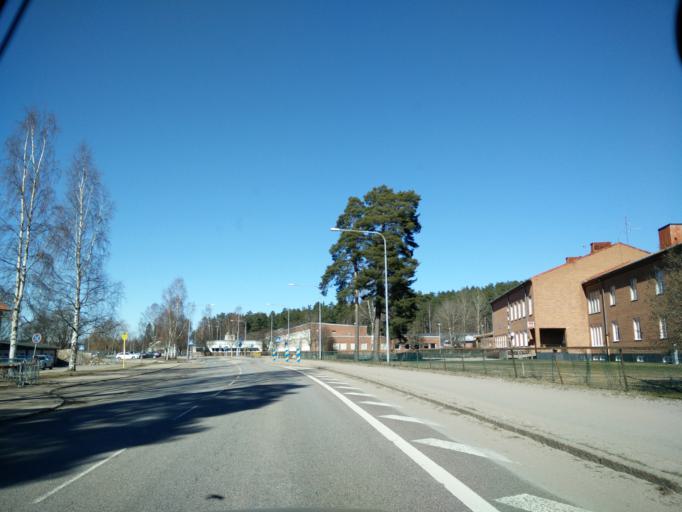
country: SE
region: Vaermland
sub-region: Hagfors Kommun
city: Hagfors
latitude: 60.0346
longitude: 13.7060
